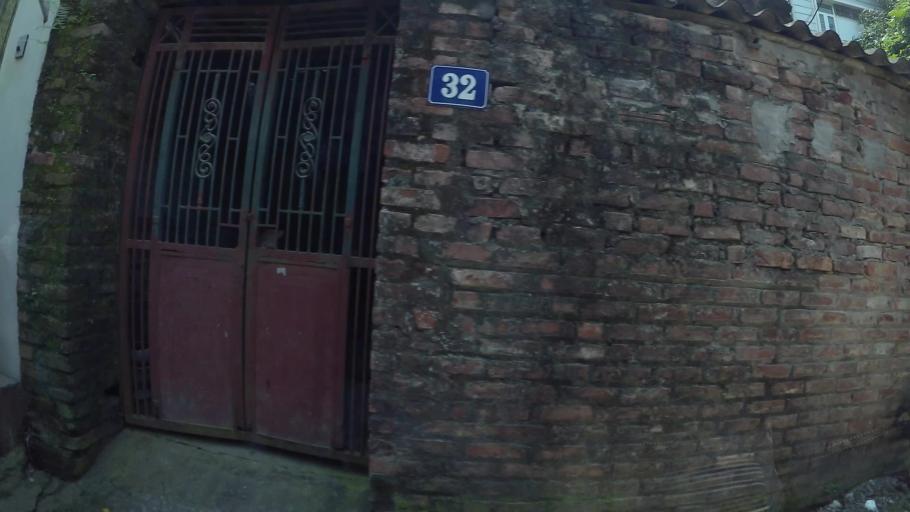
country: VN
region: Ha Noi
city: Hoan Kiem
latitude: 21.0283
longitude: 105.8860
